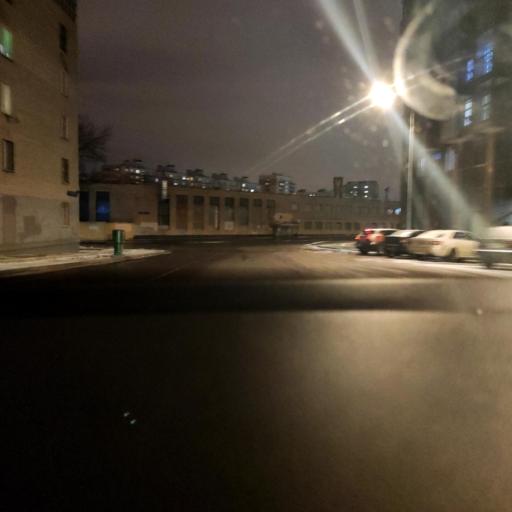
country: RU
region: Moscow
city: Tekstil'shchiki
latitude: 55.7196
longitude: 37.7269
